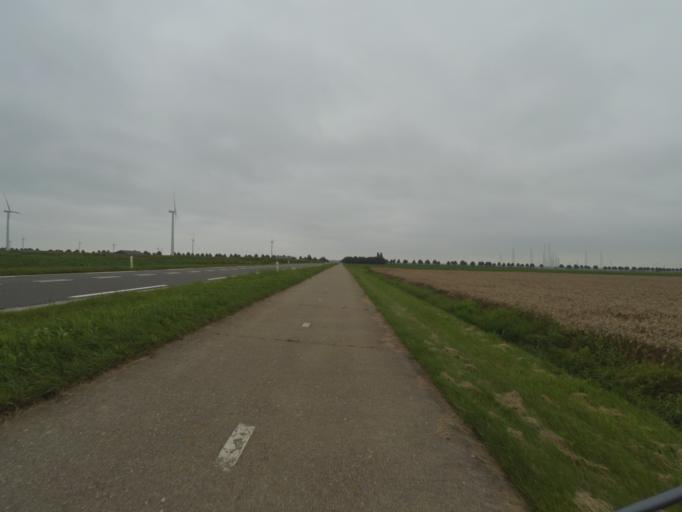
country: NL
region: Flevoland
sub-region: Gemeente Zeewolde
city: Zeewolde
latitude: 52.3744
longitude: 5.4564
